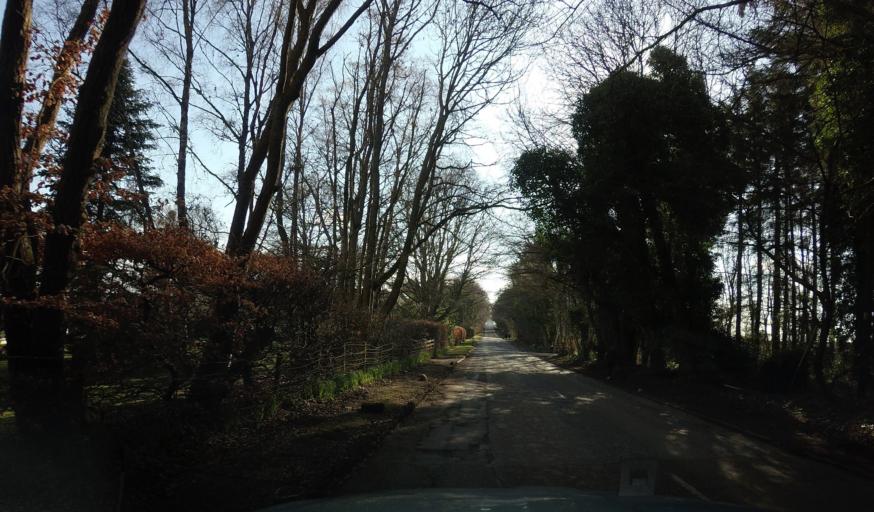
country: GB
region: Scotland
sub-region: Midlothian
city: Penicuik
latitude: 55.8477
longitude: -3.2235
